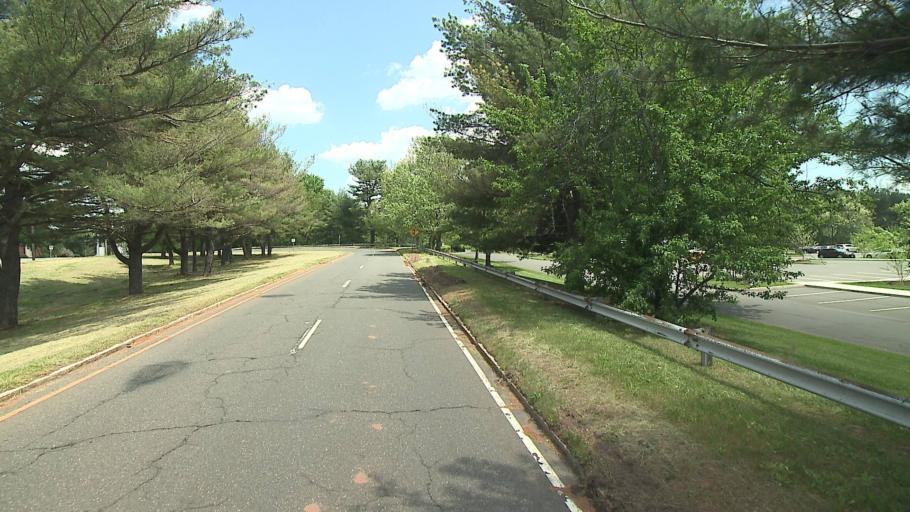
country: US
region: Connecticut
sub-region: Hartford County
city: West Hartford
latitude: 41.7285
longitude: -72.7546
